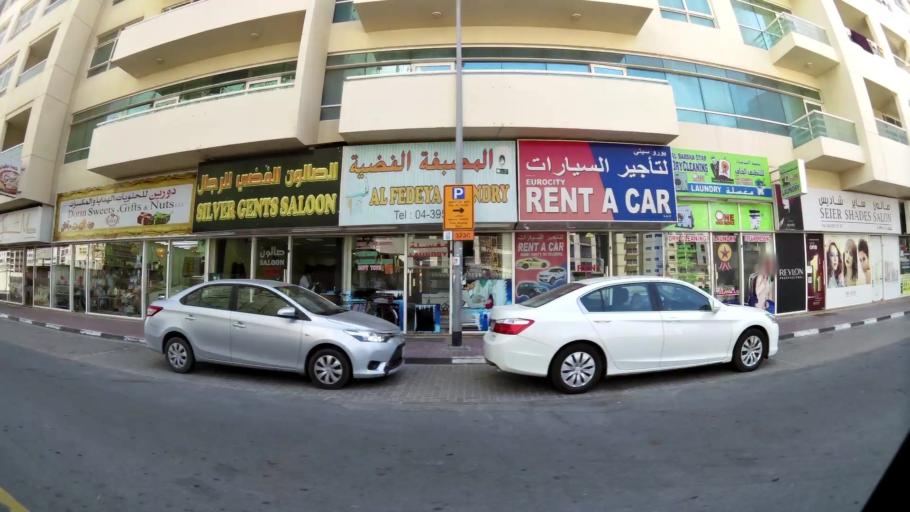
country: AE
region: Dubai
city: Dubai
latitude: 25.1128
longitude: 55.1918
